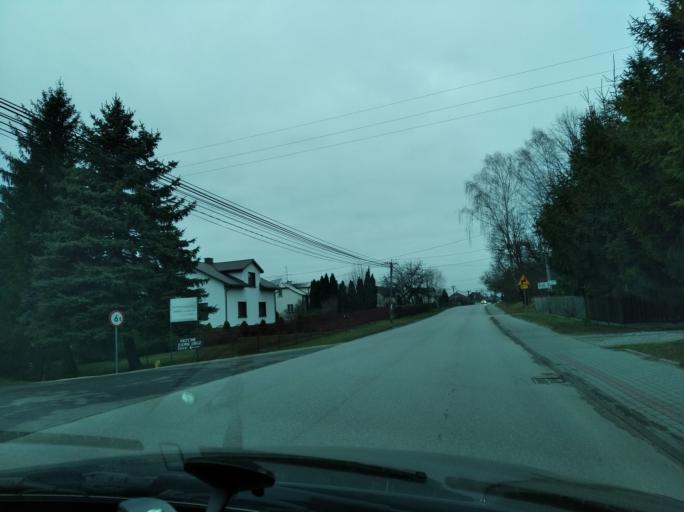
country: PL
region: Subcarpathian Voivodeship
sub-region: Powiat lancucki
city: Rakszawa
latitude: 50.1547
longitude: 22.2417
